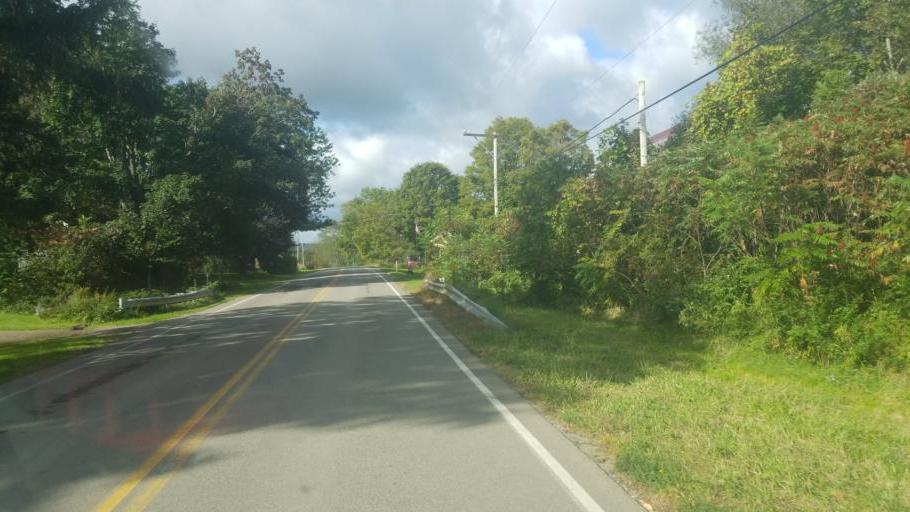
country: US
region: New York
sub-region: Allegany County
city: Cuba
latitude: 42.1534
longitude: -78.2915
